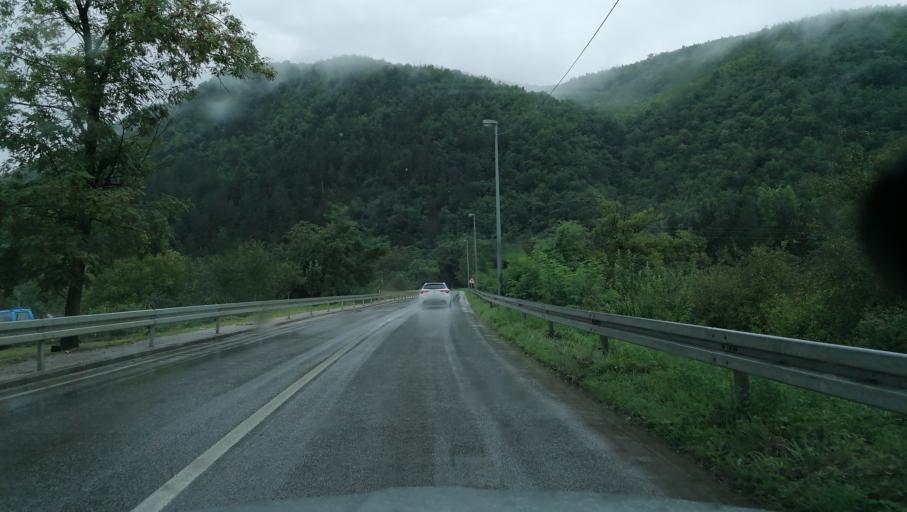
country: BA
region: Federation of Bosnia and Herzegovina
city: Gorazde
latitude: 43.6790
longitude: 19.0142
